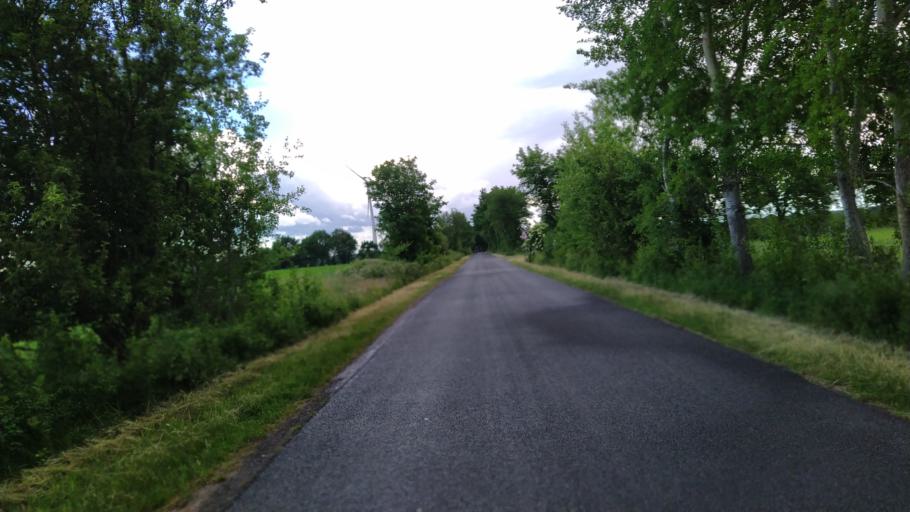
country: DE
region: Lower Saxony
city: Sandbostel
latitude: 53.4262
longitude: 9.1675
